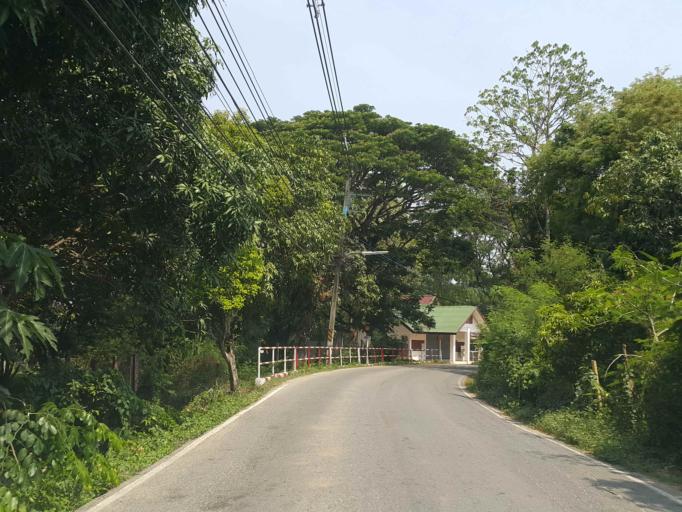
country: TH
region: Chiang Mai
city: San Sai
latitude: 18.8737
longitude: 98.9783
